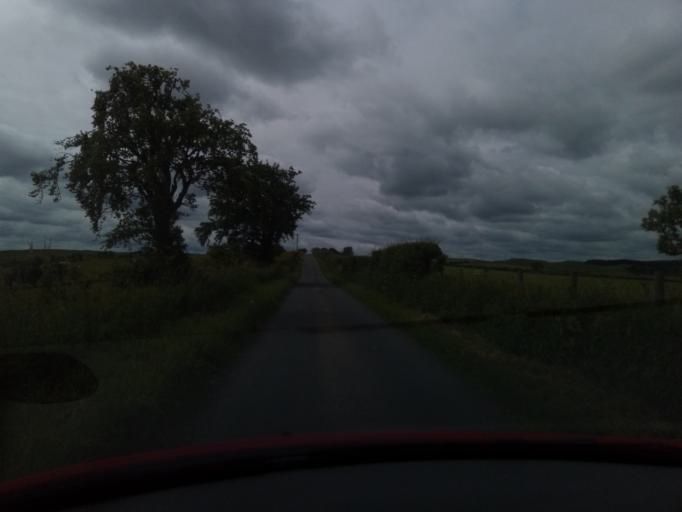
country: GB
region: Scotland
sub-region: The Scottish Borders
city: Hawick
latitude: 55.4519
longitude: -2.7953
